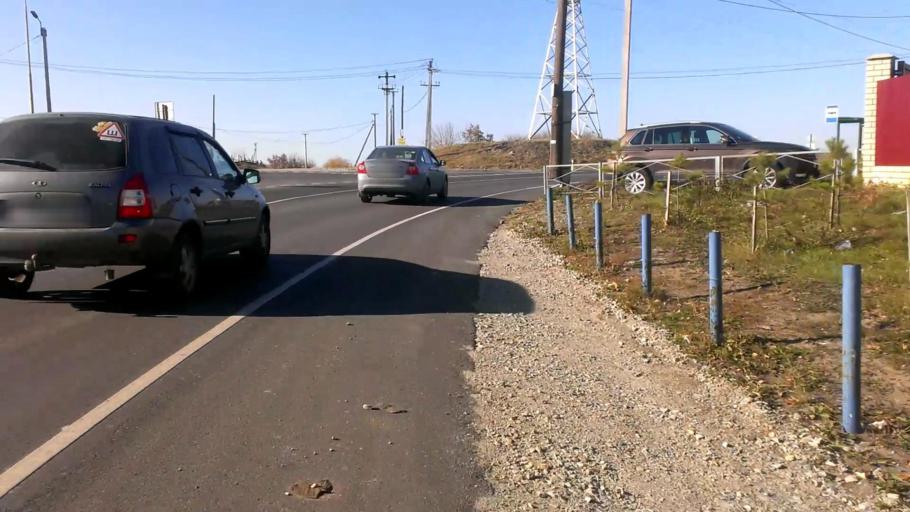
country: RU
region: Altai Krai
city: Sannikovo
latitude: 53.3182
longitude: 83.9449
